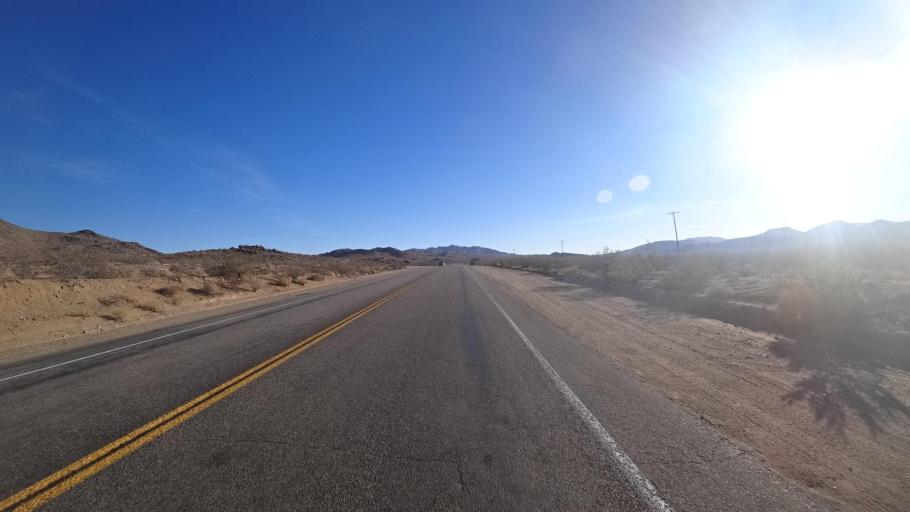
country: US
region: California
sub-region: Kern County
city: Ridgecrest
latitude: 35.5564
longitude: -117.7136
